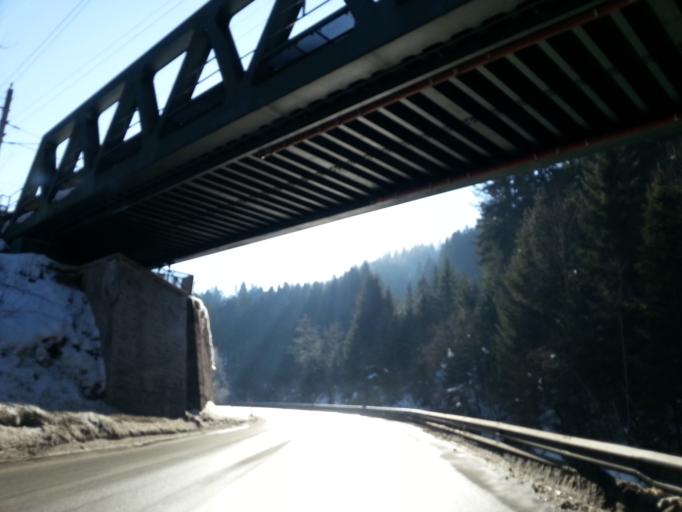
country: AT
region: Salzburg
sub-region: Politischer Bezirk Sankt Johann im Pongau
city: Huttau
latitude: 47.4216
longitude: 13.3479
